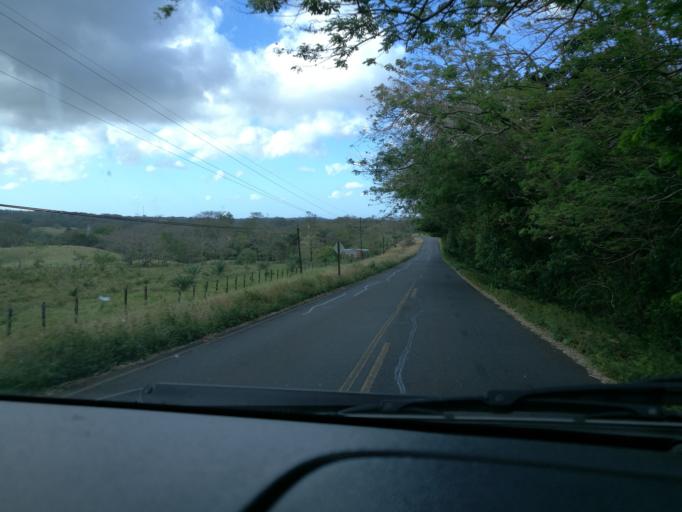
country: CR
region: Alajuela
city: Bijagua
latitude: 10.6637
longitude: -85.0912
